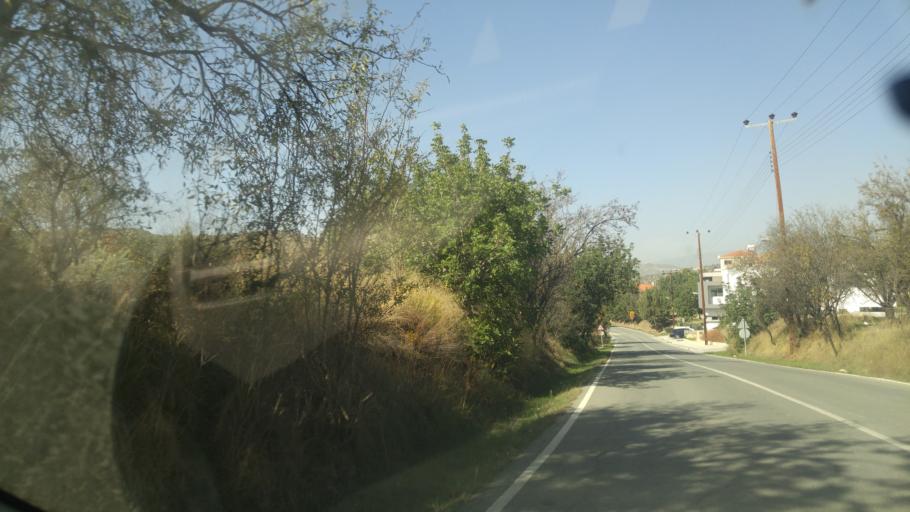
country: CY
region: Limassol
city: Pano Polemidia
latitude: 34.7564
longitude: 33.0308
